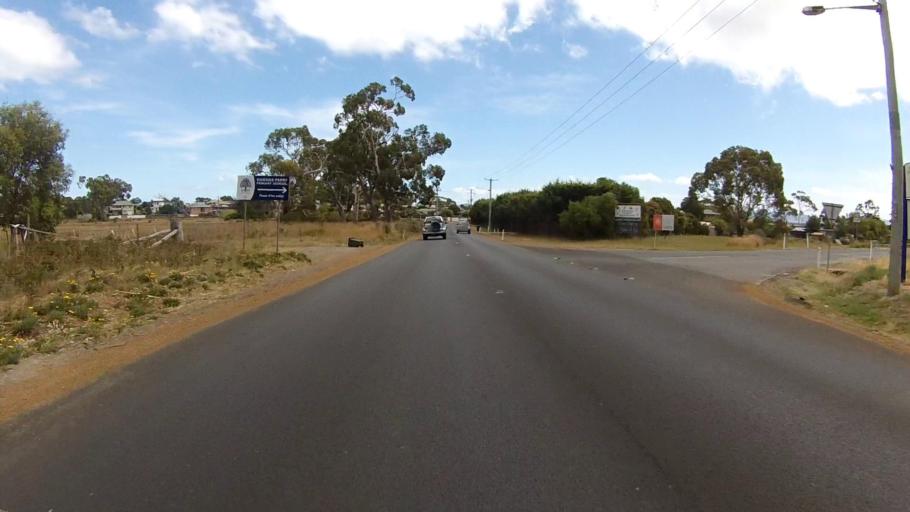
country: AU
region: Tasmania
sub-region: Sorell
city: Sorell
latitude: -42.8500
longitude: 147.6255
